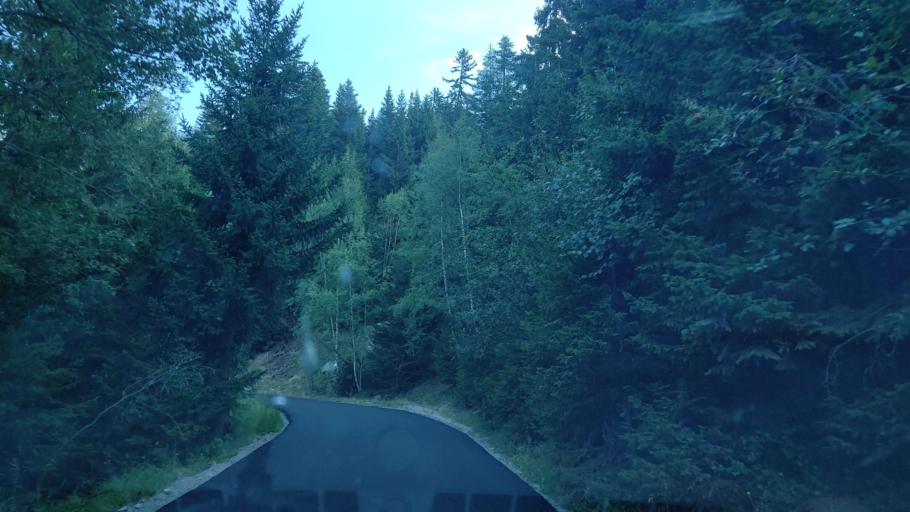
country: FR
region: Rhone-Alpes
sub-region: Departement de la Savoie
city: Val Thorens
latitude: 45.2237
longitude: 6.5554
